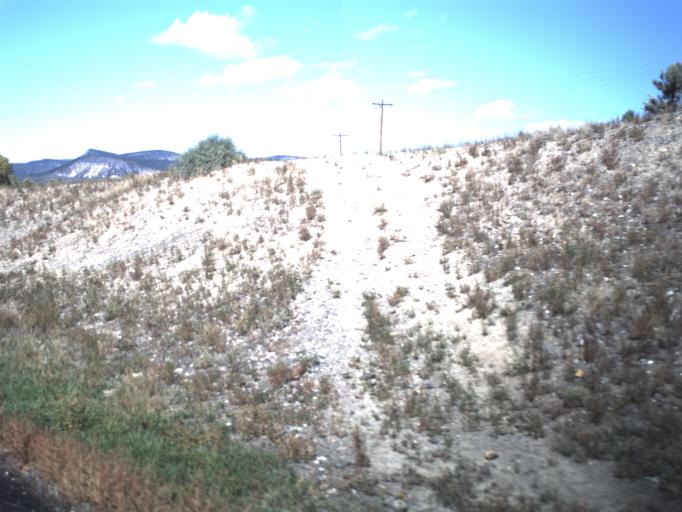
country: US
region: Utah
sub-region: Piute County
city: Junction
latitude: 38.1534
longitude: -112.0033
